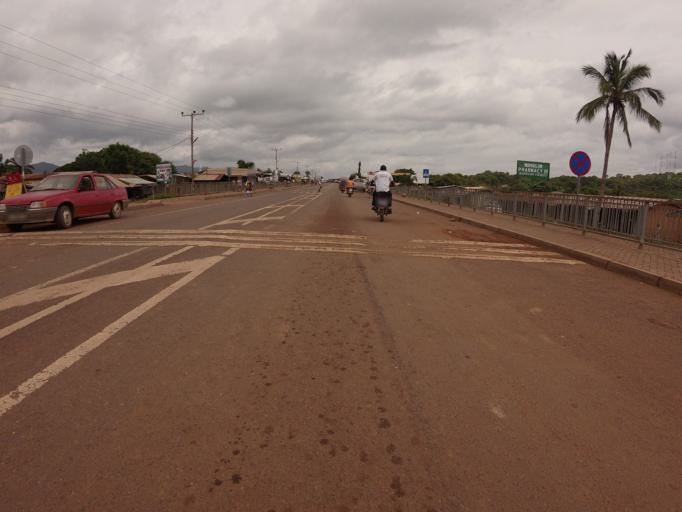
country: TG
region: Centrale
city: Sotouboua
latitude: 8.2656
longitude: 0.5201
